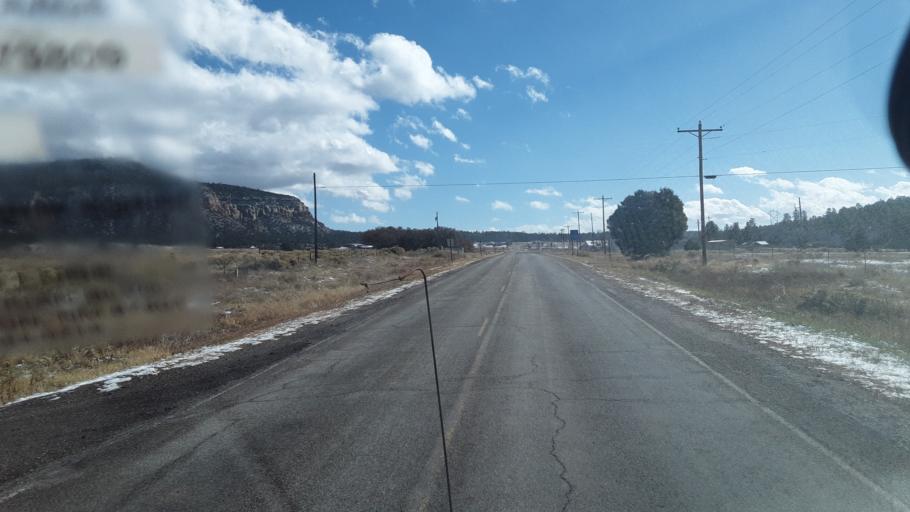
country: US
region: New Mexico
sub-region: Rio Arriba County
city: Santa Teresa
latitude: 36.2238
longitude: -106.7948
